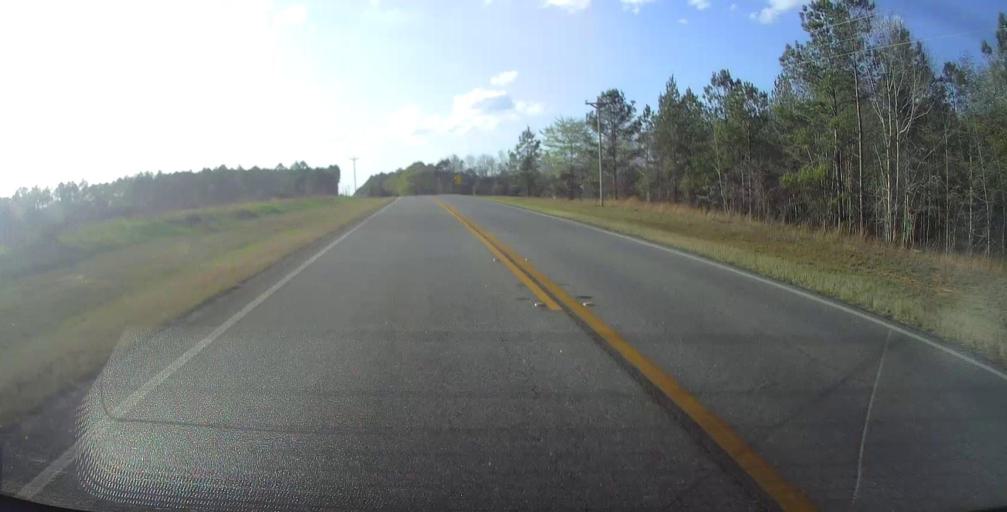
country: US
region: Georgia
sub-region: Tattnall County
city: Reidsville
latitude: 32.1344
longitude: -82.2259
